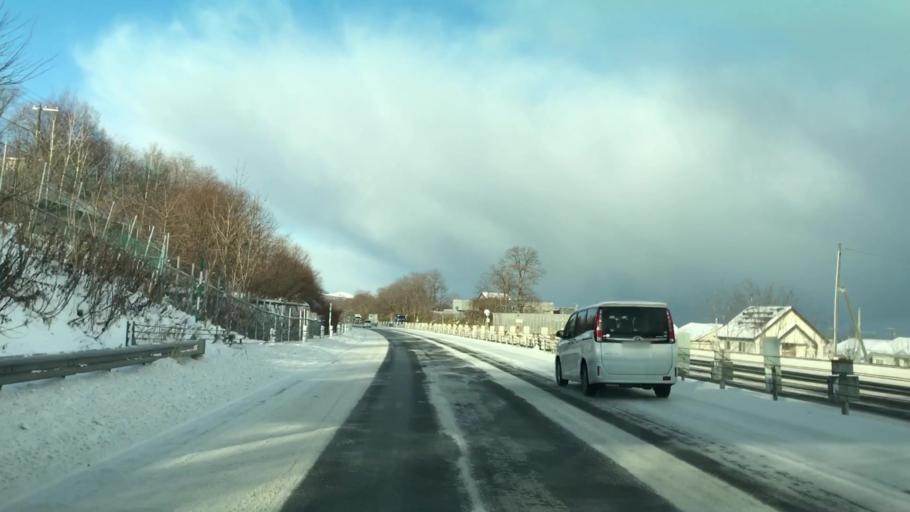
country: JP
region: Hokkaido
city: Sapporo
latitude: 43.1172
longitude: 141.2309
